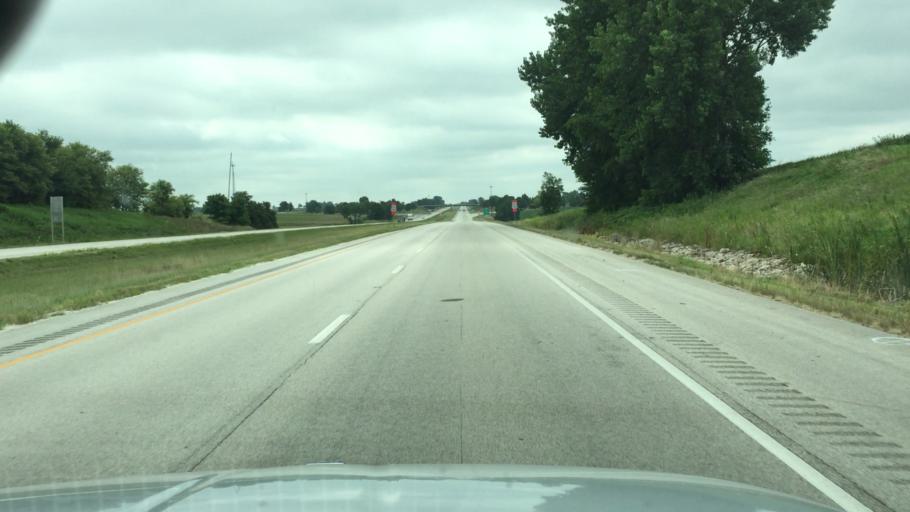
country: US
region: Illinois
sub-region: Henry County
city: Orion
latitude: 41.3056
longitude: -90.3341
